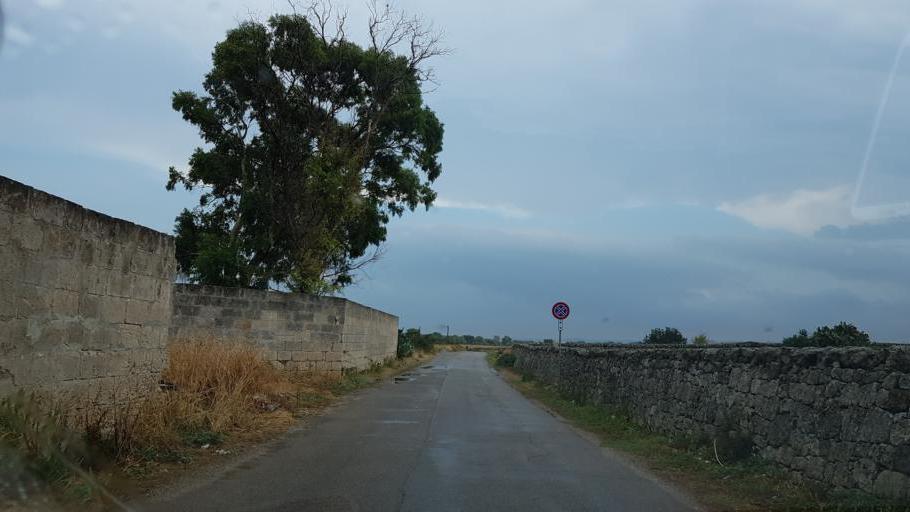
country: IT
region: Apulia
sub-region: Provincia di Bari
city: Monopoli
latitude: 40.9327
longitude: 17.3231
